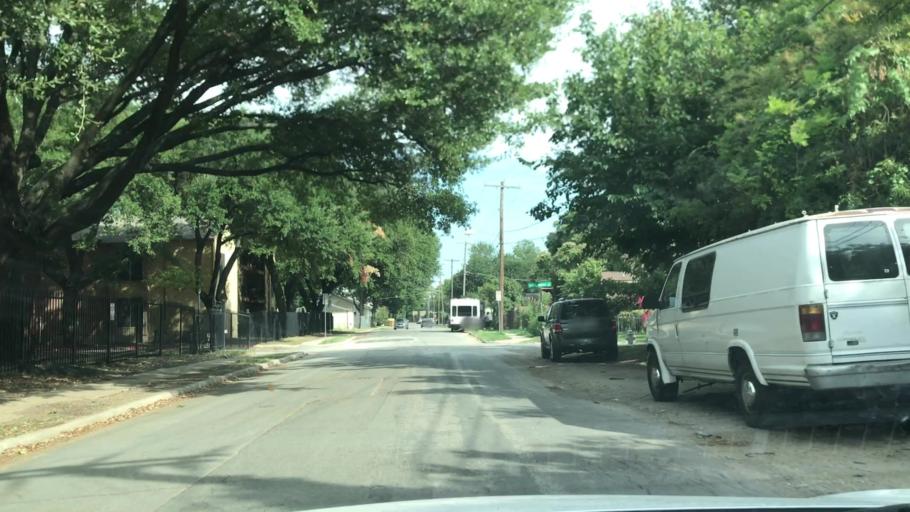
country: US
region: Texas
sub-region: Dallas County
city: Highland Park
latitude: 32.8122
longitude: -96.7869
